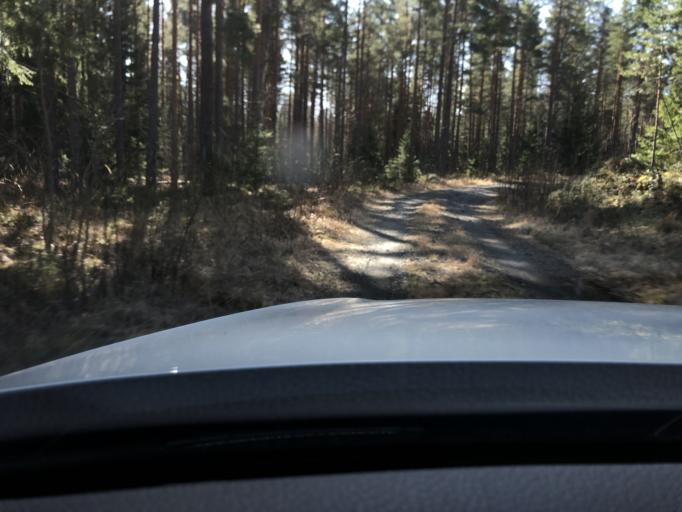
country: SE
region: Uppsala
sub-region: Heby Kommun
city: OEstervala
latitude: 60.3308
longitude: 17.1768
